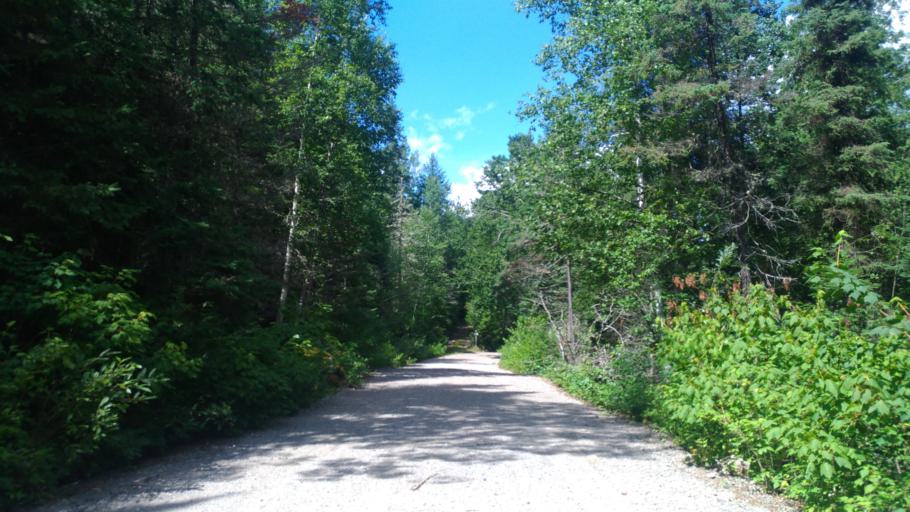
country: CA
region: Ontario
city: Rayside-Balfour
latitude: 46.5893
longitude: -81.5470
